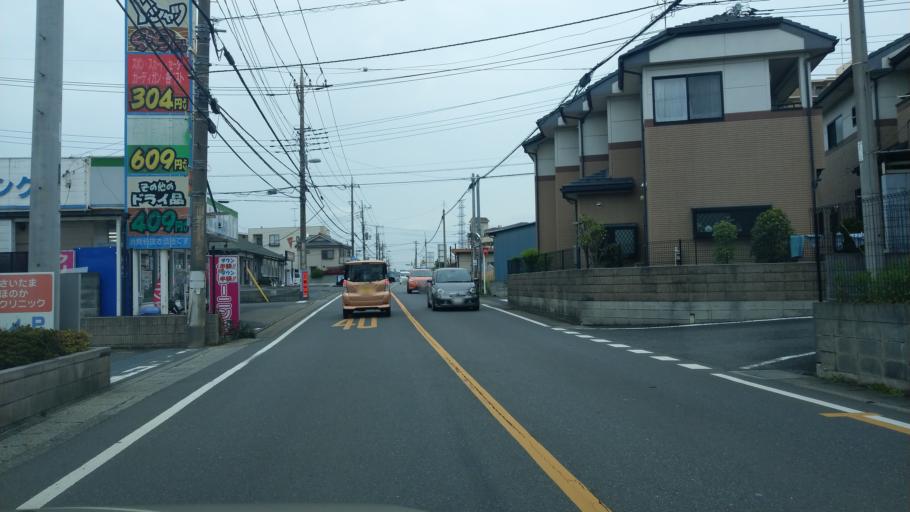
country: JP
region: Saitama
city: Iwatsuki
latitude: 35.9371
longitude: 139.6748
